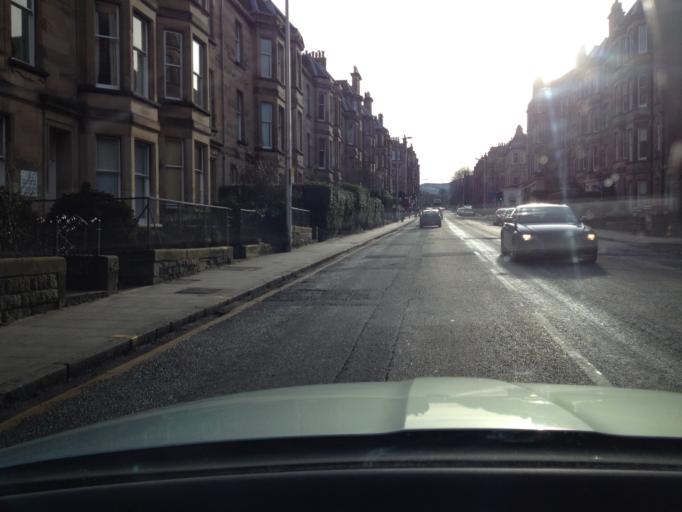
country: GB
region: Scotland
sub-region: Edinburgh
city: Edinburgh
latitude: 55.9235
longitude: -3.2105
